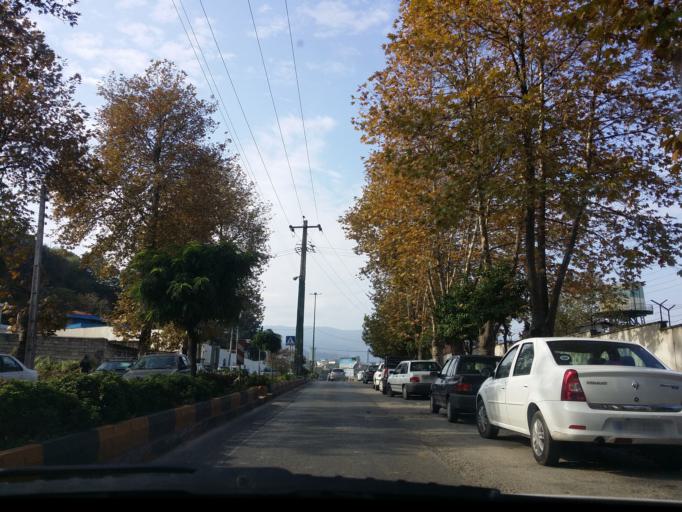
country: IR
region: Mazandaran
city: Chalus
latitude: 36.6495
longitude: 51.4163
